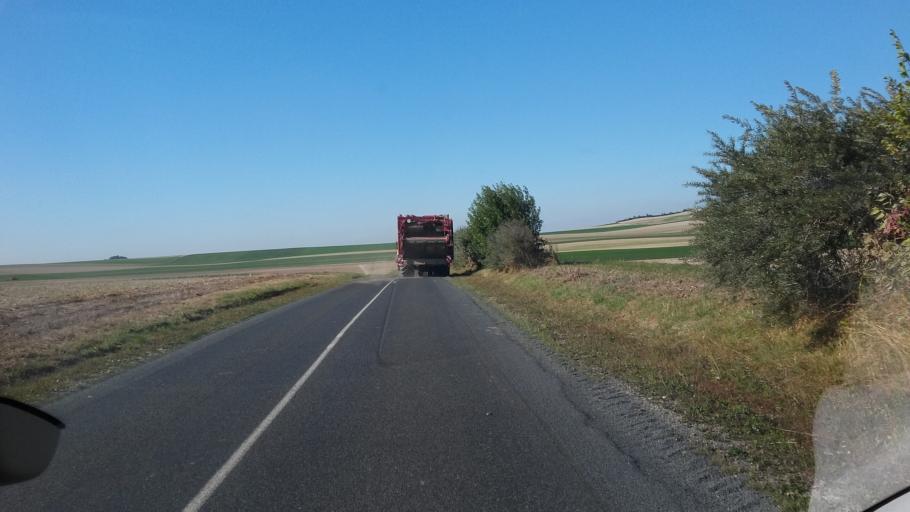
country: FR
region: Champagne-Ardenne
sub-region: Departement de la Marne
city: Connantre
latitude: 48.7499
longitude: 3.8858
